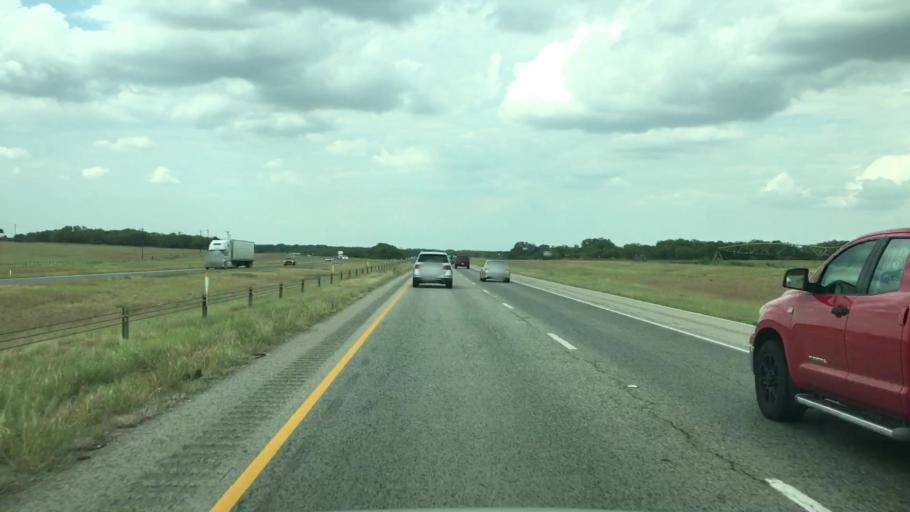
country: US
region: Texas
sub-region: Atascosa County
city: Pleasanton
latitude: 29.0179
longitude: -98.4310
